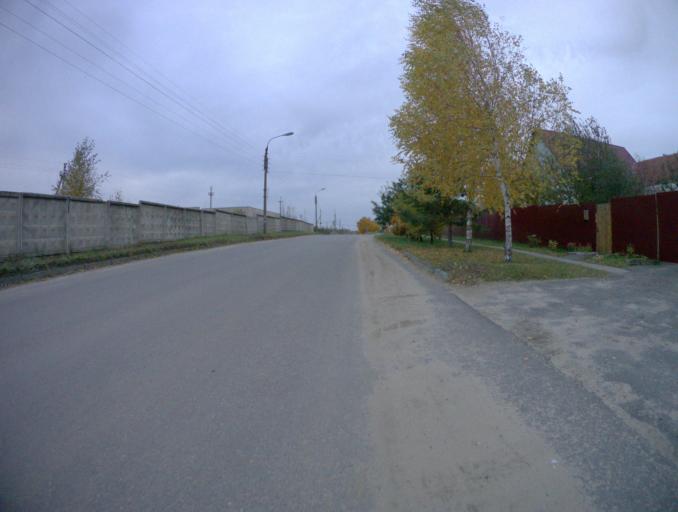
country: RU
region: Vladimir
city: Kommunar
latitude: 56.0590
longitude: 40.4858
